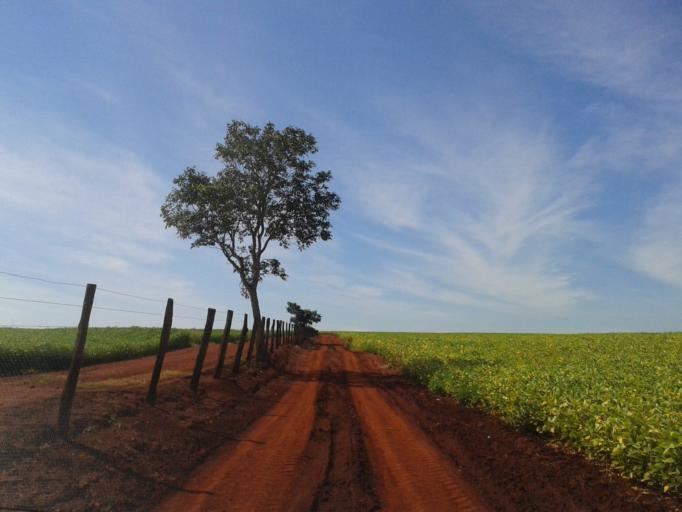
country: BR
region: Minas Gerais
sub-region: Capinopolis
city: Capinopolis
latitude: -18.6384
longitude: -49.7276
